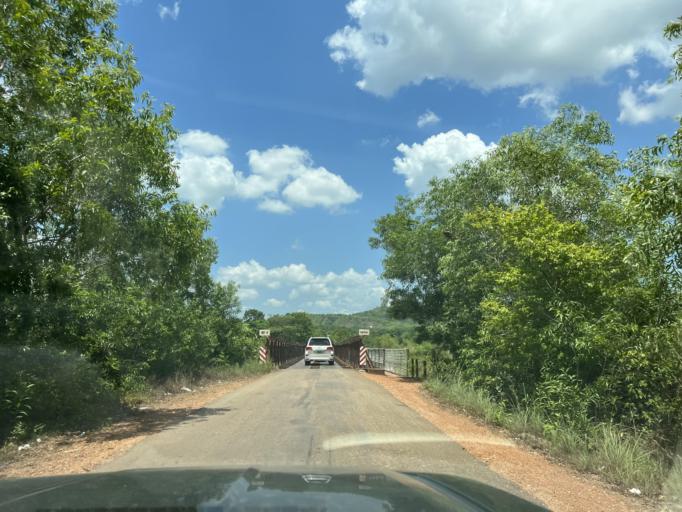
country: MM
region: Tanintharyi
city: Dawei
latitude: 14.6115
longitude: 98.0241
